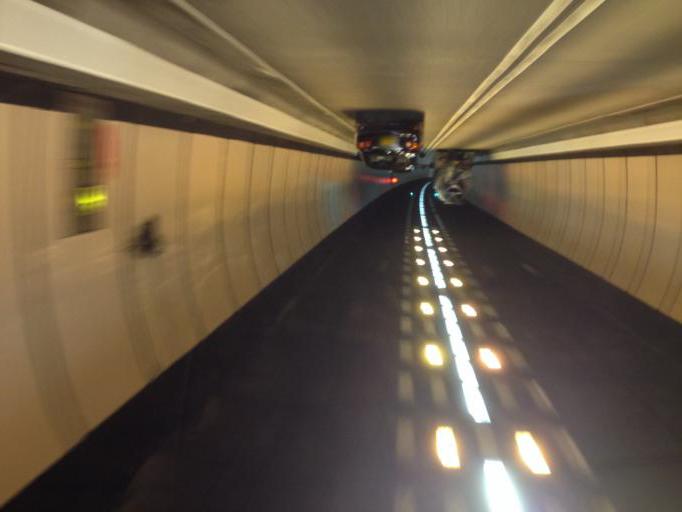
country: HK
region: Wong Tai Sin
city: Wong Tai Sin
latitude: 22.3421
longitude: 114.2046
